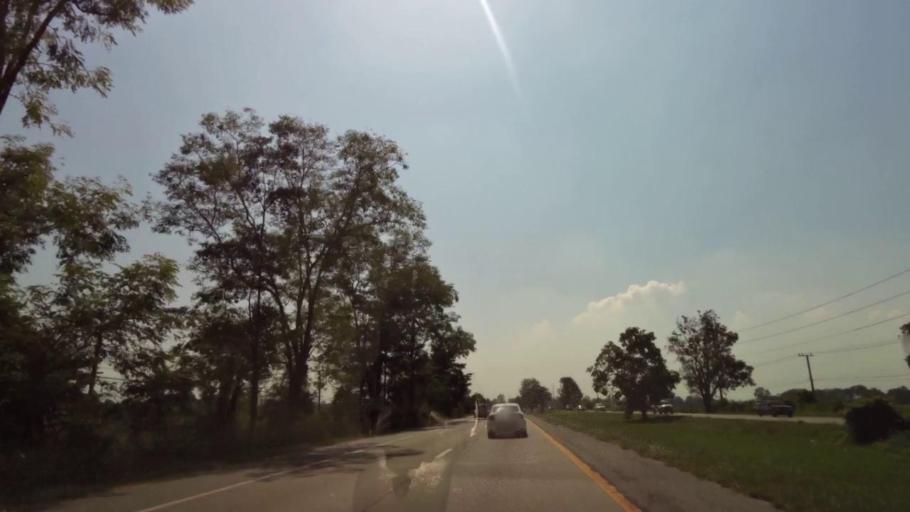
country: TH
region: Phichit
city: Wachira Barami
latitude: 16.5946
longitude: 100.1477
